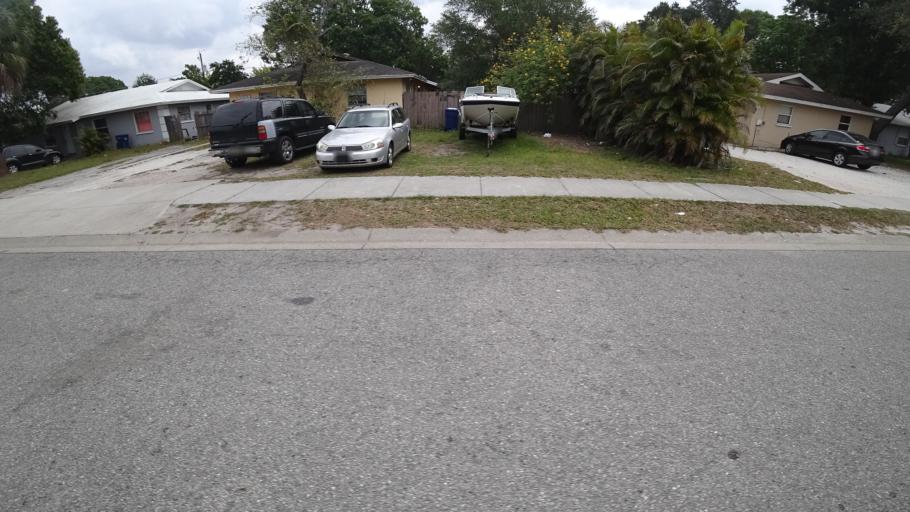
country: US
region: Florida
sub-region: Manatee County
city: West Samoset
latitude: 27.4650
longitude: -82.5569
